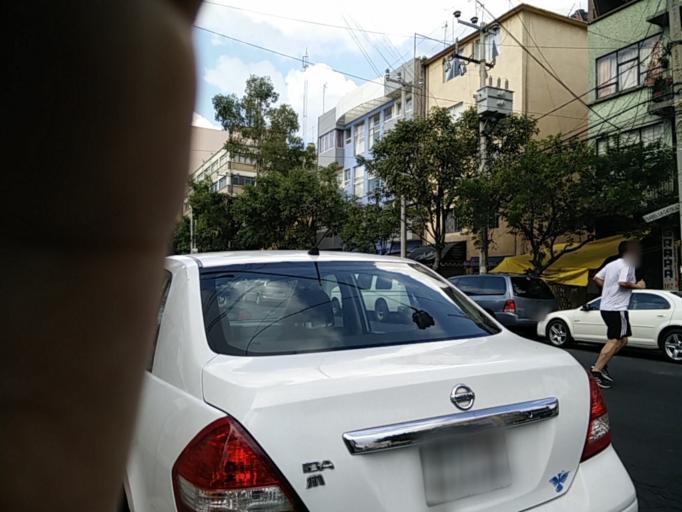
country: MX
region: Mexico City
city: Benito Juarez
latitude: 19.4086
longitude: -99.1395
